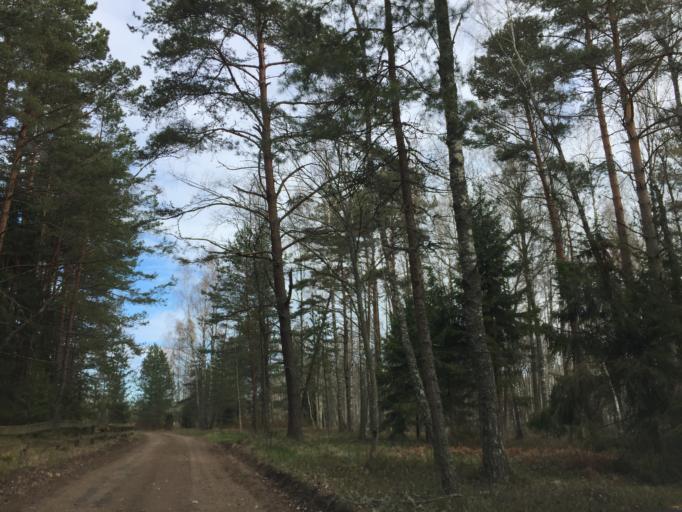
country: LV
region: Salacgrivas
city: Salacgriva
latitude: 57.5402
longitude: 24.3675
